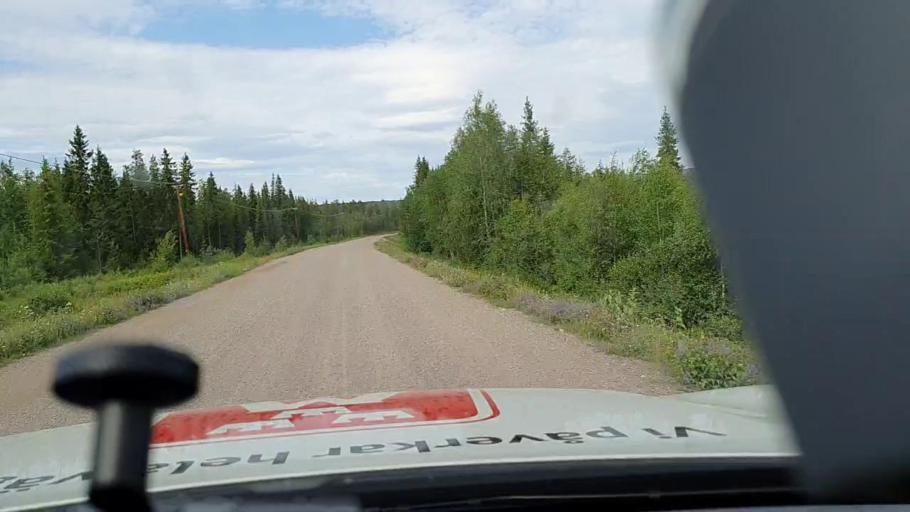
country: SE
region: Norrbotten
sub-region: Alvsbyns Kommun
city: AElvsbyn
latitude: 66.1163
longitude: 20.9753
